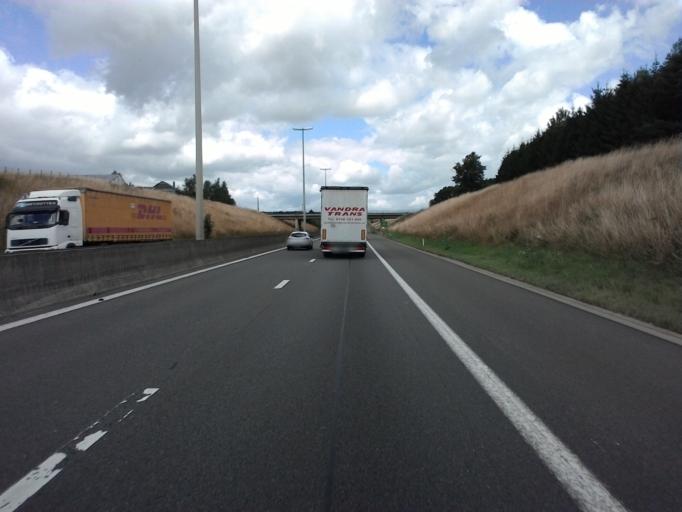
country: BE
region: Wallonia
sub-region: Province du Luxembourg
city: Leglise
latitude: 49.7965
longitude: 5.5239
